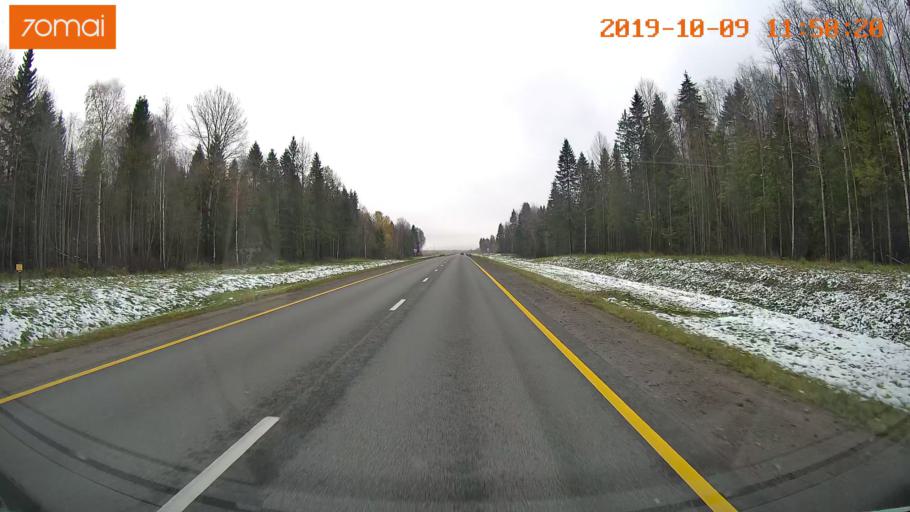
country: RU
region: Vologda
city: Gryazovets
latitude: 58.8068
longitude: 40.2447
